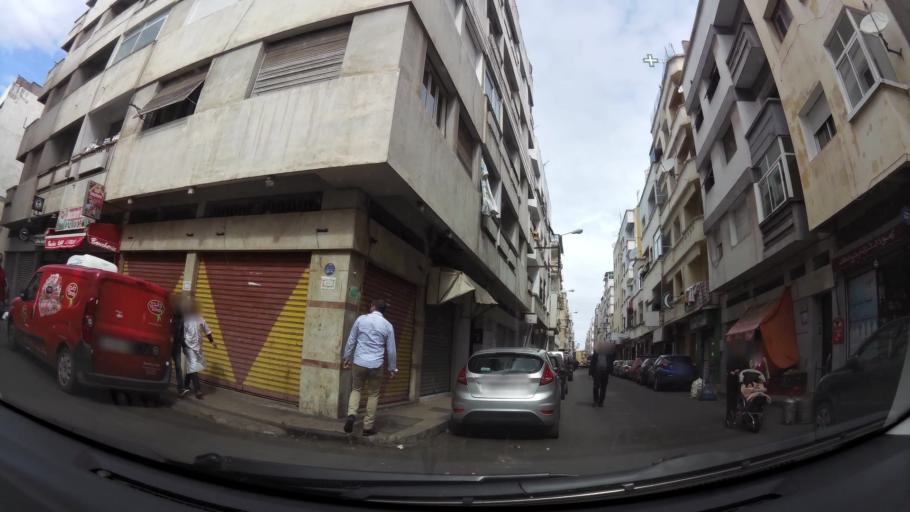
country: MA
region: Grand Casablanca
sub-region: Casablanca
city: Casablanca
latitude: 33.5816
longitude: -7.6369
